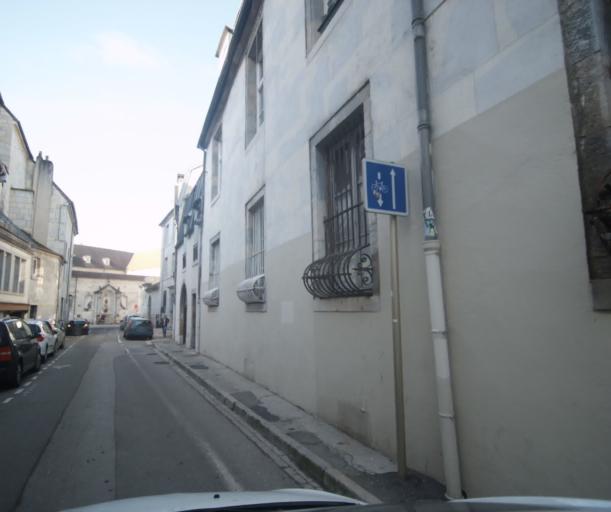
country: FR
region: Franche-Comte
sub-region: Departement du Doubs
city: Besancon
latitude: 47.2378
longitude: 6.0218
